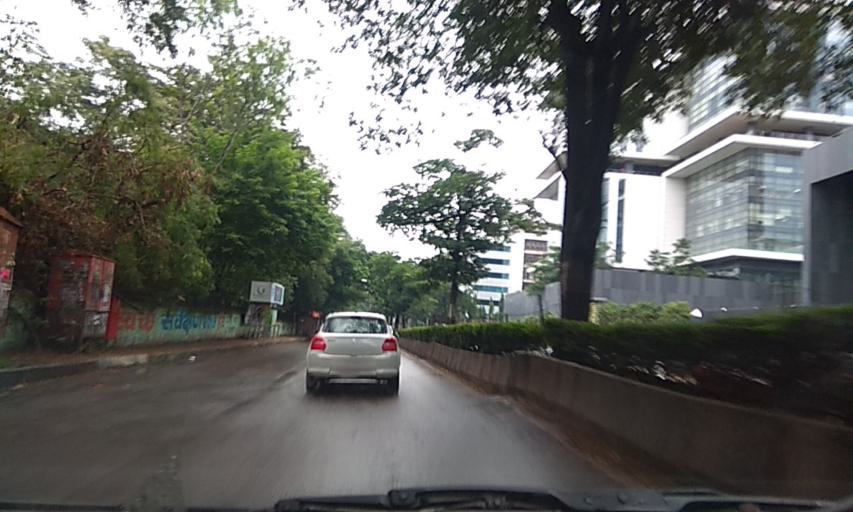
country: IN
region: Maharashtra
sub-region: Pune Division
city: Khadki
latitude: 18.5520
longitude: 73.8897
